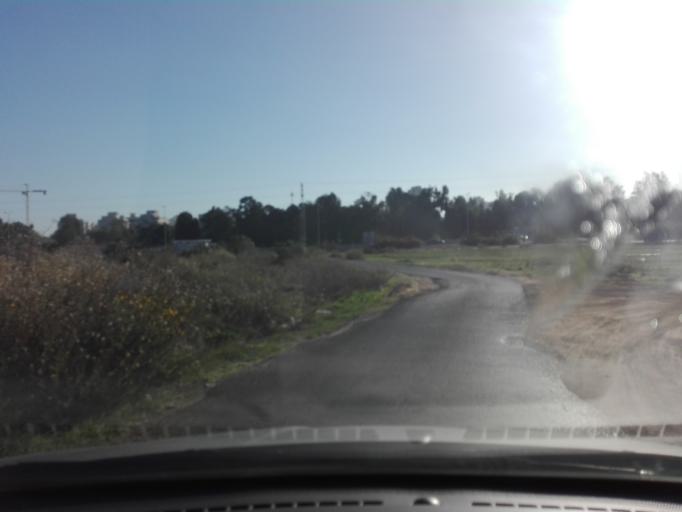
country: IL
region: Central District
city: Netanya
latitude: 32.3086
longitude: 34.8634
